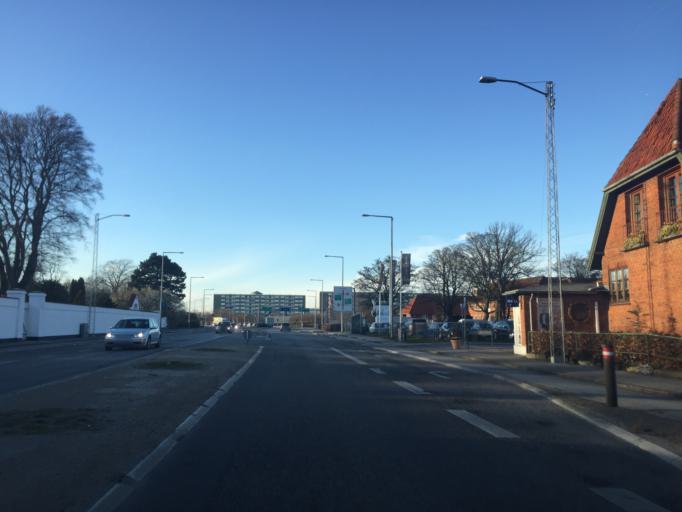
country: DK
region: Capital Region
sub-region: Tarnby Kommune
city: Tarnby
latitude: 55.6271
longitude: 12.6041
